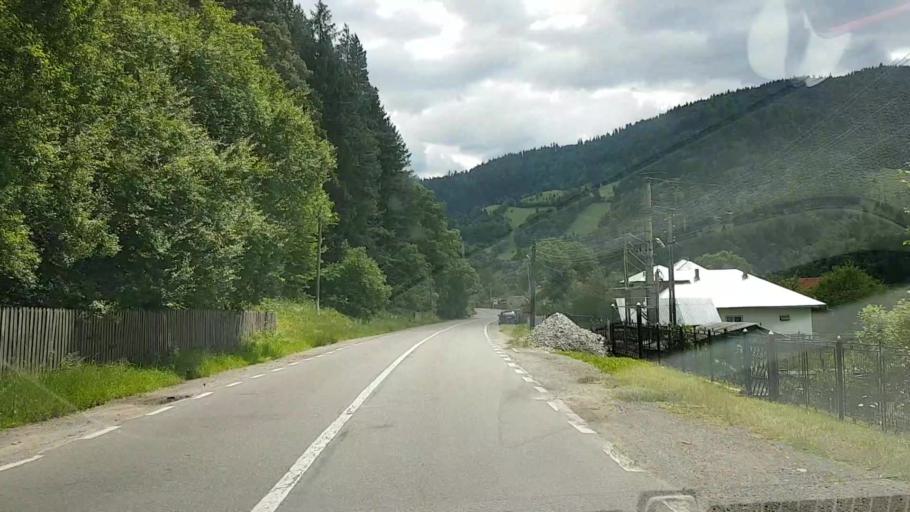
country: RO
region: Neamt
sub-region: Comuna Poiana Teiului
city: Poiana Teiului
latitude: 47.1261
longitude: 25.9066
